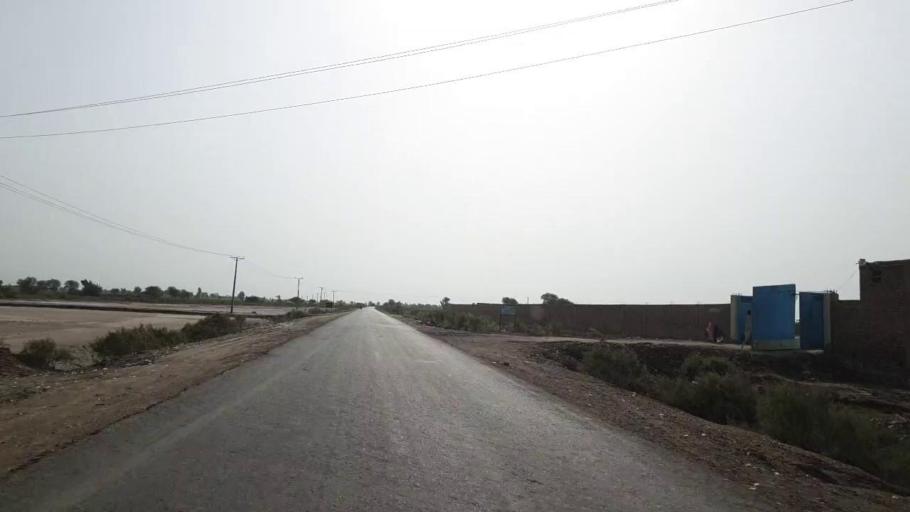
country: PK
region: Sindh
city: Jam Sahib
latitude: 26.2808
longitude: 68.5777
